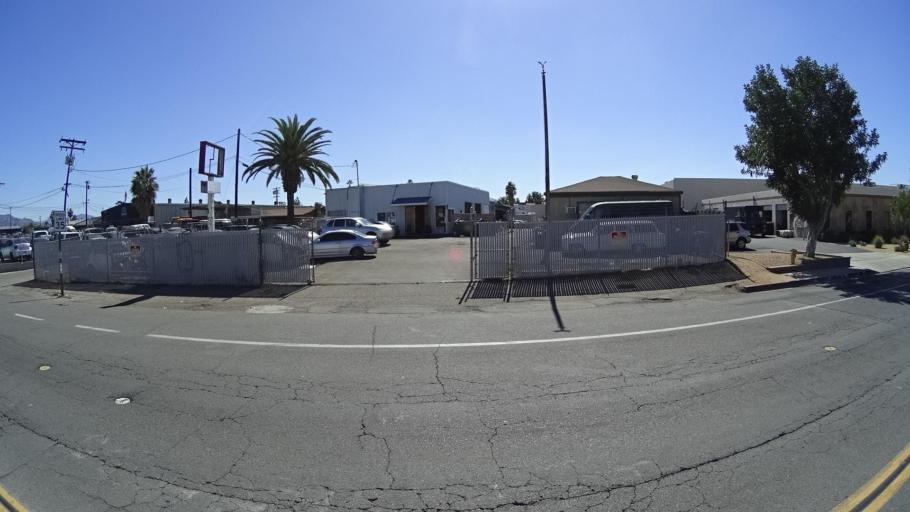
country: US
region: California
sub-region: San Diego County
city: El Cajon
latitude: 32.8125
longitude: -116.9660
